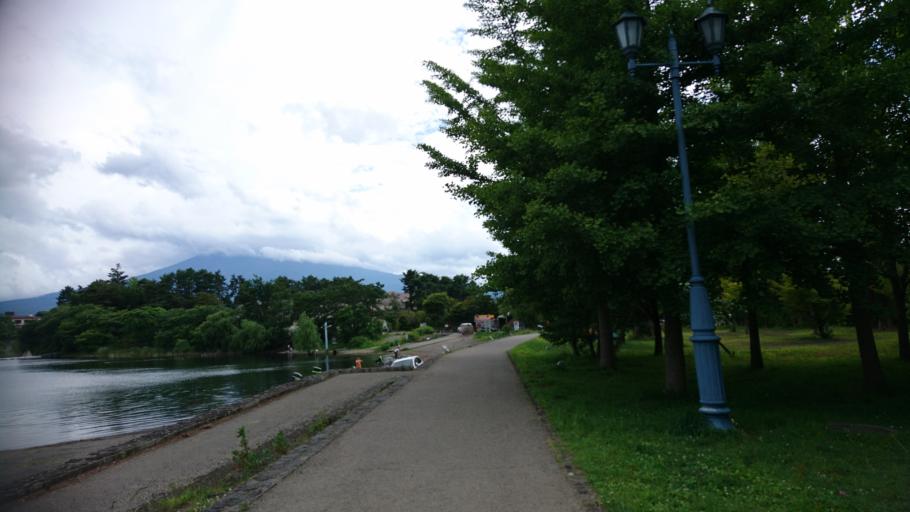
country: JP
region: Yamanashi
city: Fujikawaguchiko
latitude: 35.5073
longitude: 138.7637
